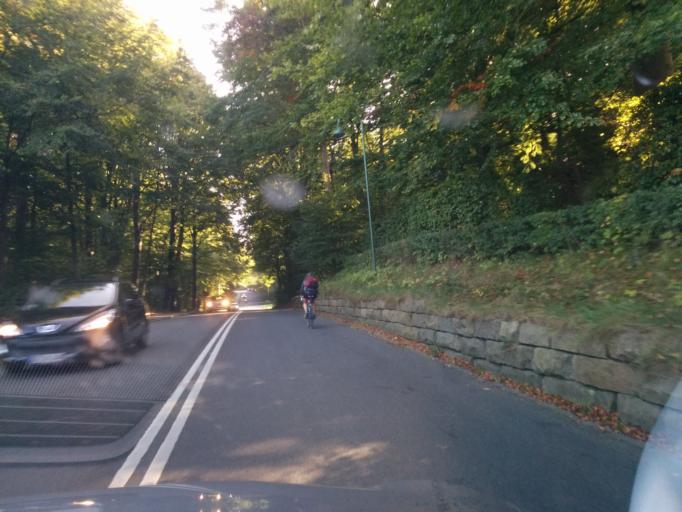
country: DK
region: Central Jutland
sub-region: Arhus Kommune
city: Arhus
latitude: 56.1273
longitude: 10.2053
